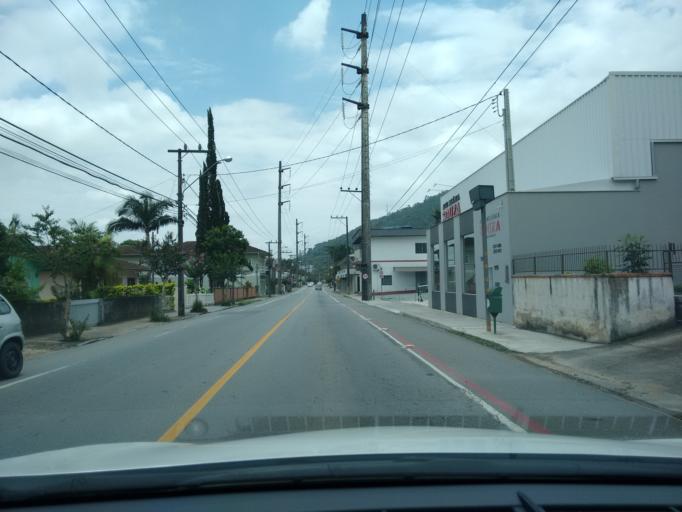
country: BR
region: Santa Catarina
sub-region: Jaragua Do Sul
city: Jaragua do Sul
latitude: -26.4960
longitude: -49.0764
